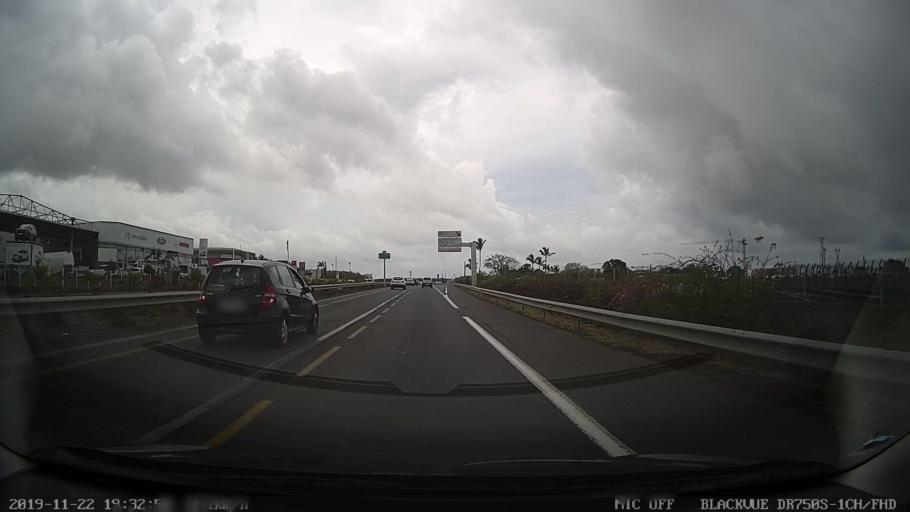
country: RE
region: Reunion
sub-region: Reunion
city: Le Port
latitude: -20.9538
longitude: 55.3145
